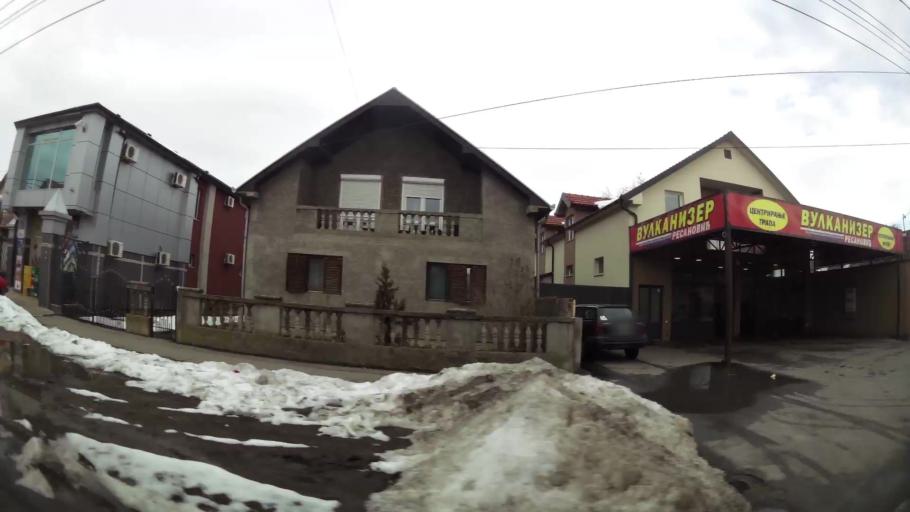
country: RS
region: Central Serbia
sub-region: Belgrade
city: Surcin
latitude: 44.7924
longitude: 20.2773
